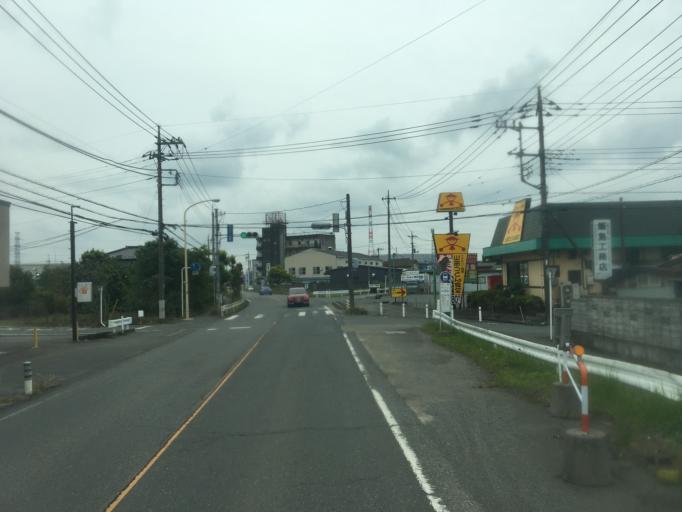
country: JP
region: Saitama
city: Sakado
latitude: 35.9828
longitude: 139.4542
